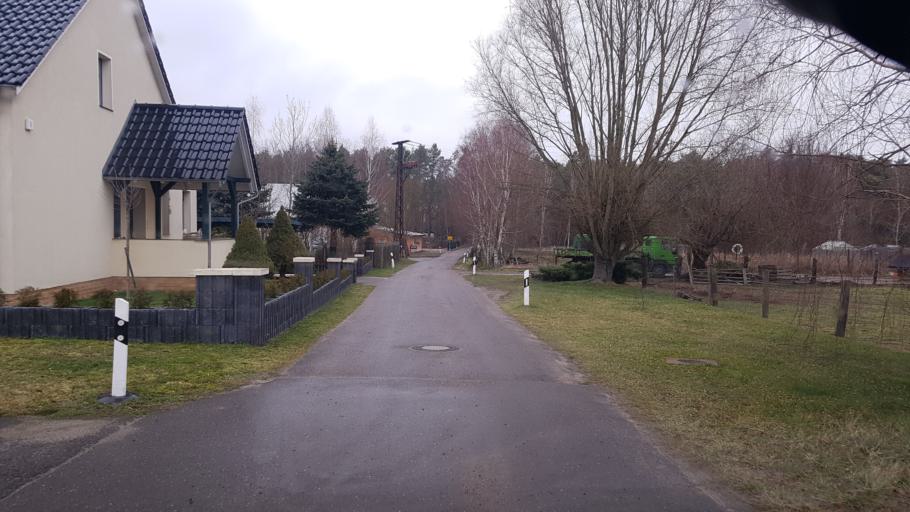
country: DE
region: Brandenburg
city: Crinitz
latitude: 51.7468
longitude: 13.7774
